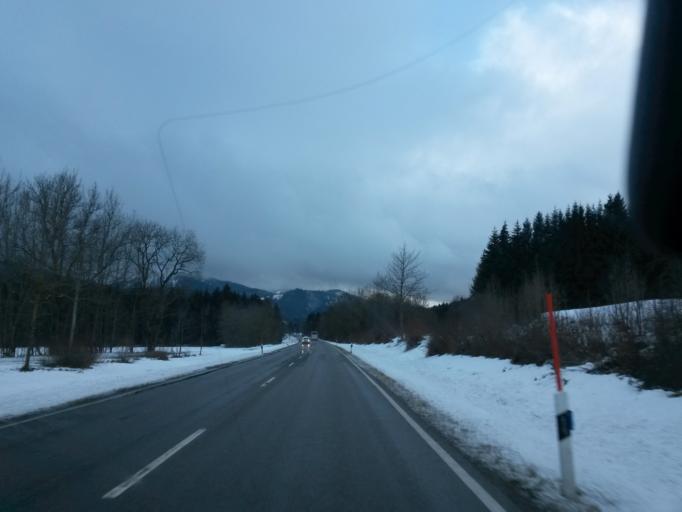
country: DE
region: Bavaria
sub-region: Swabia
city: Oy-Mittelberg
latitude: 47.6175
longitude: 10.4366
